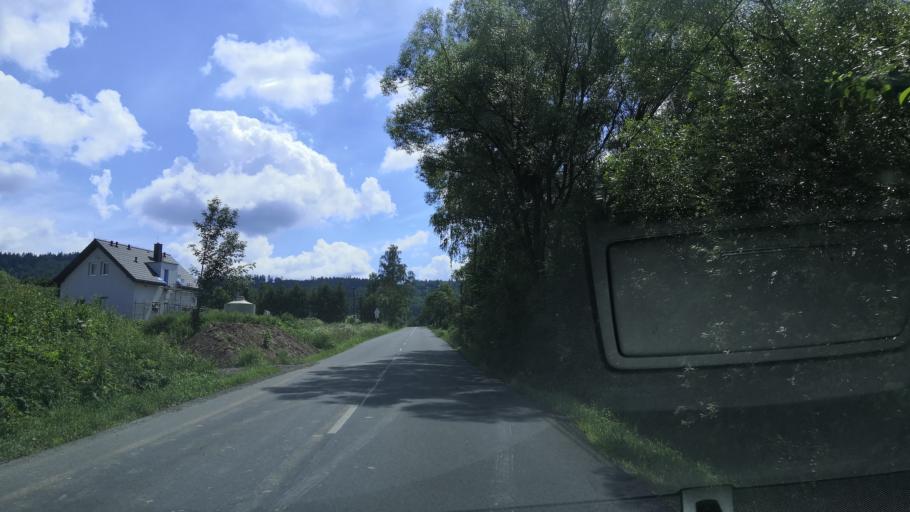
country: CZ
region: Zlin
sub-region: Okres Vsetin
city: Roznov pod Radhostem
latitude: 49.4455
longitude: 18.1381
